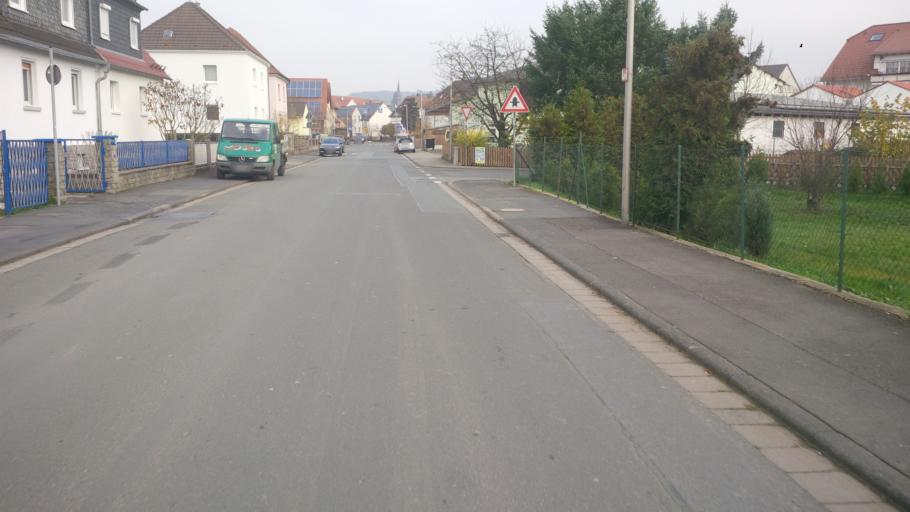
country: DE
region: Hesse
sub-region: Regierungsbezirk Darmstadt
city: Wehrheim
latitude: 50.3004
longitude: 8.5668
